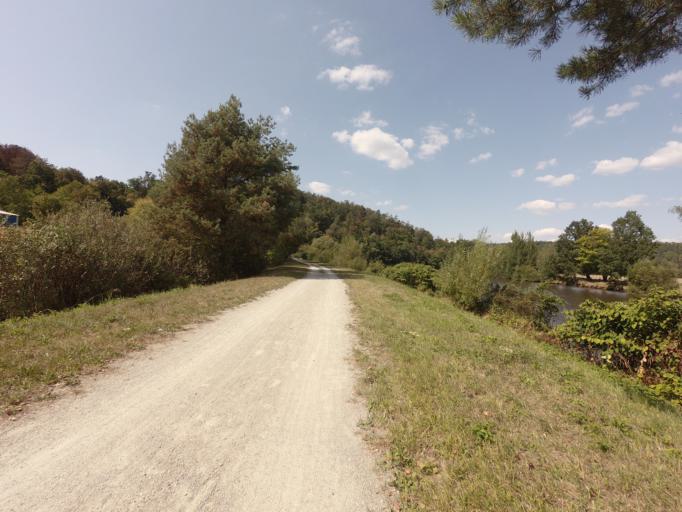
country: CZ
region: Jihocesky
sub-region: Okres Ceske Budejovice
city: Hluboka nad Vltavou
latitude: 49.0564
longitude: 14.4433
